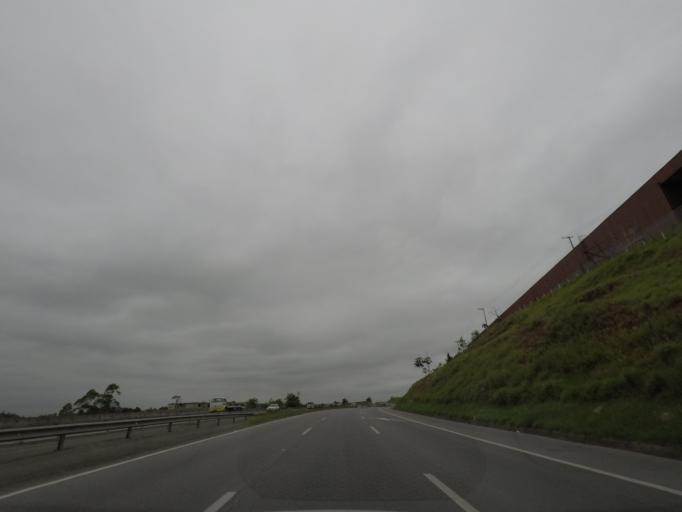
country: BR
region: Sao Paulo
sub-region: Jacarei
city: Jacarei
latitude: -23.2684
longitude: -46.0604
